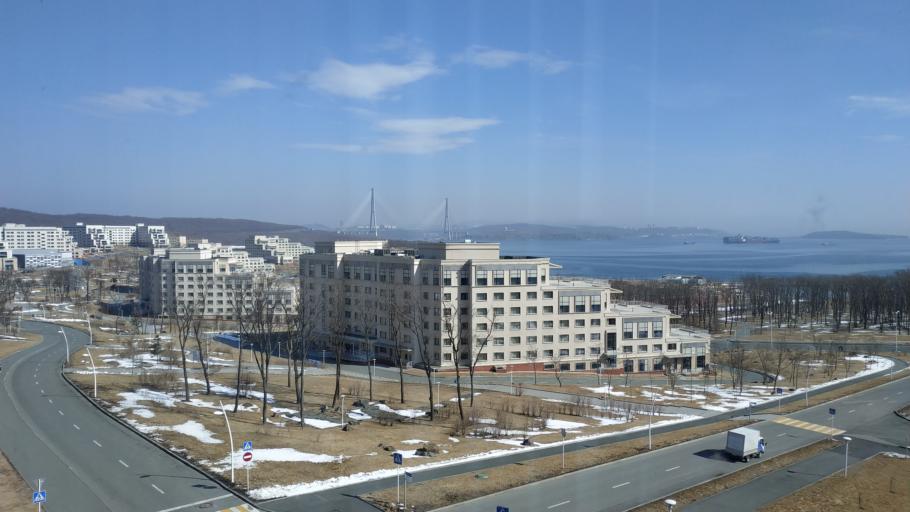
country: RU
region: Primorskiy
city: Russkiy
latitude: 43.0264
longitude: 131.8881
